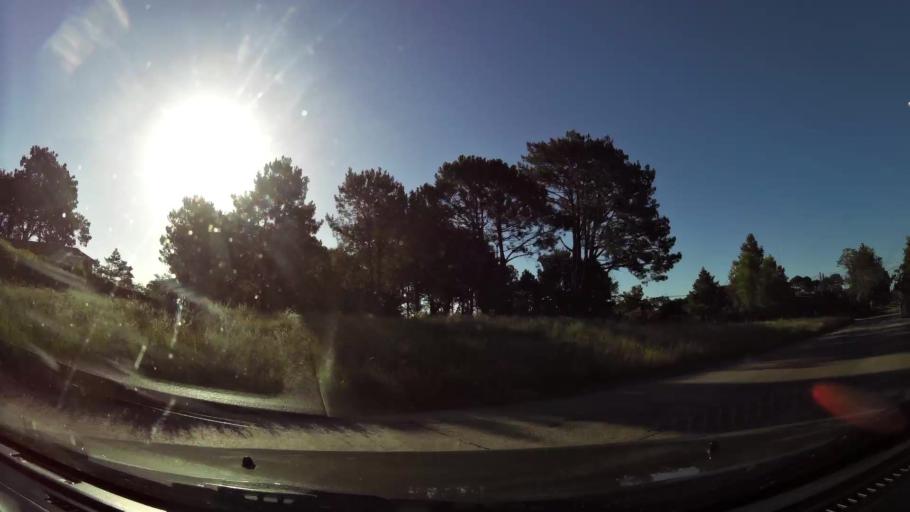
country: UY
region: Canelones
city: Paso de Carrasco
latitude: -34.8732
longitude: -56.0517
